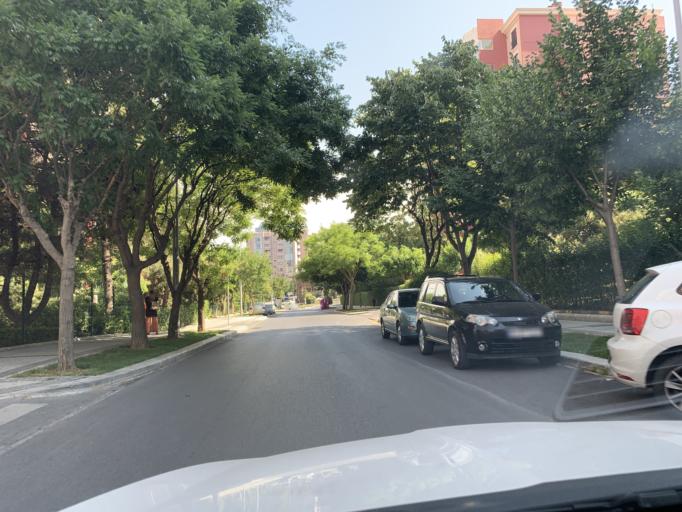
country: TR
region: Istanbul
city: Esenyurt
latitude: 41.0653
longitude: 28.6818
